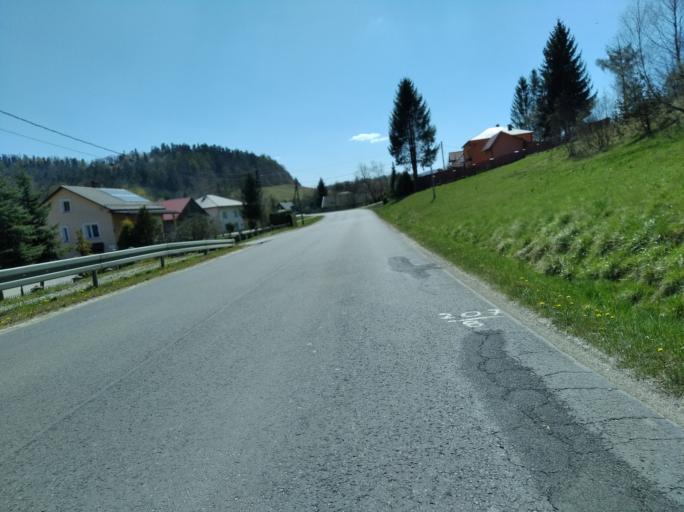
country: PL
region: Subcarpathian Voivodeship
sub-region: Powiat brzozowski
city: Dydnia
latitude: 49.6886
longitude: 22.1862
